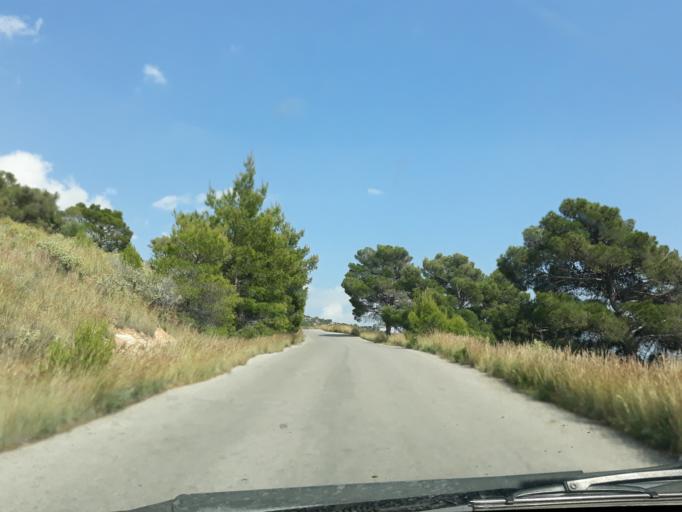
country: GR
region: Attica
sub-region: Nomarchia Dytikis Attikis
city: Fyli
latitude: 38.0944
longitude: 23.6362
